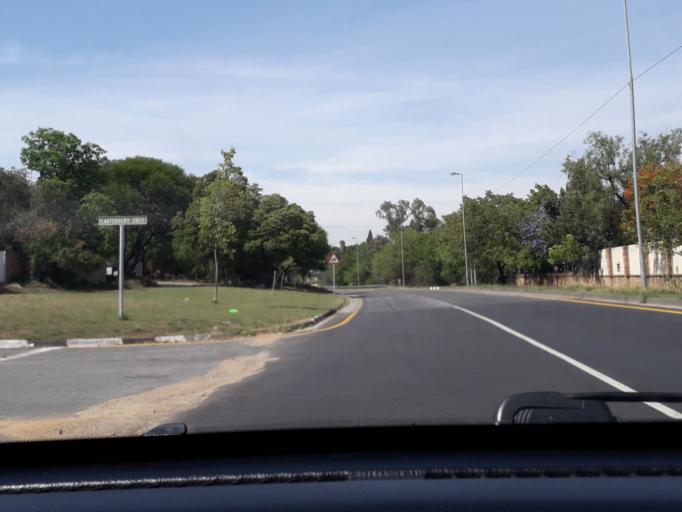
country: ZA
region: Gauteng
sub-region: City of Johannesburg Metropolitan Municipality
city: Midrand
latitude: -26.0567
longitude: 28.0709
